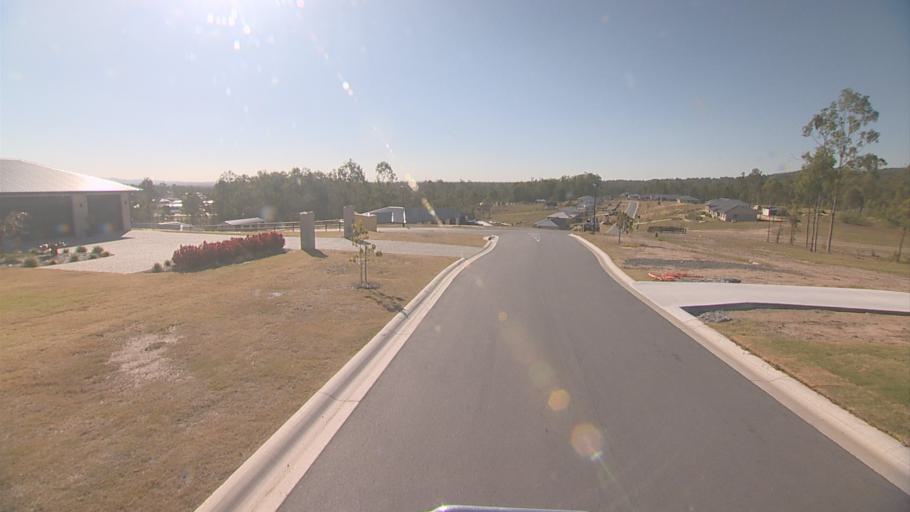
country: AU
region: Queensland
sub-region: Logan
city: Cedar Vale
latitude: -27.8716
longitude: 153.0520
